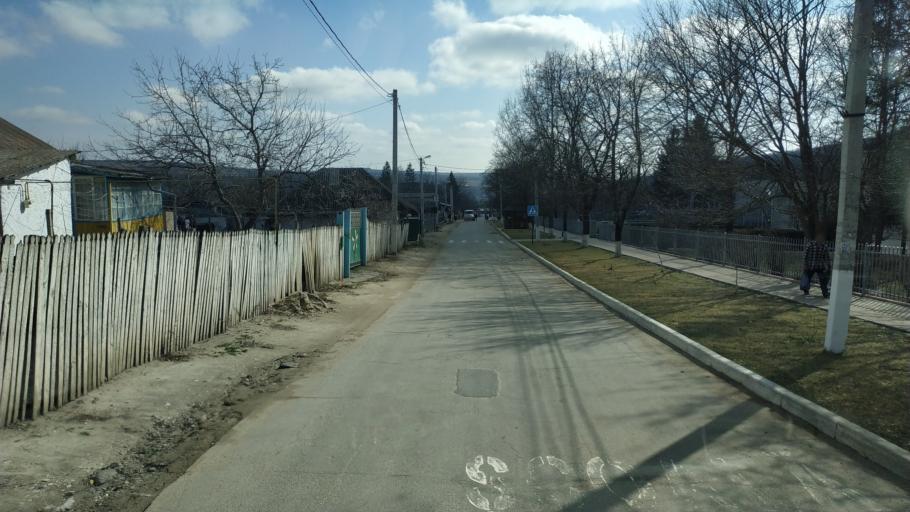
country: MD
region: Hincesti
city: Hincesti
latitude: 46.8277
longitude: 28.6710
